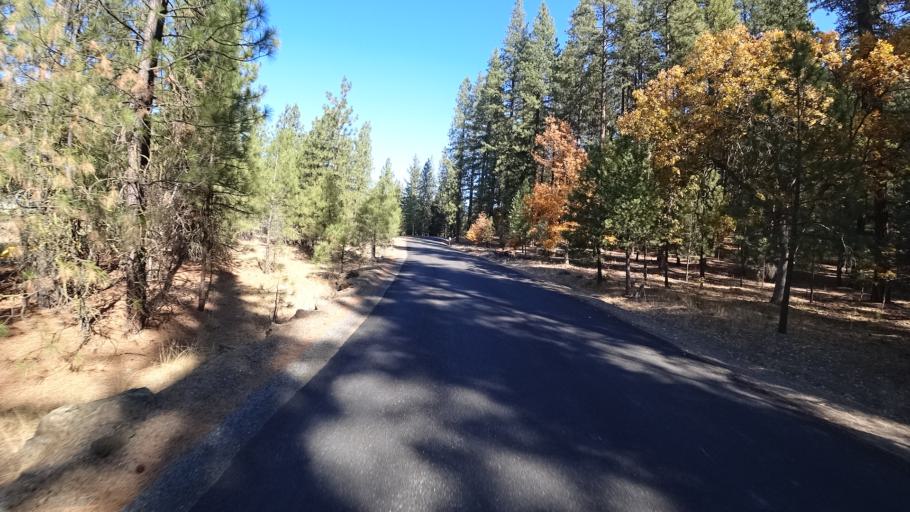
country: US
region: California
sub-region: Siskiyou County
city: Yreka
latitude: 41.6460
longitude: -122.8695
